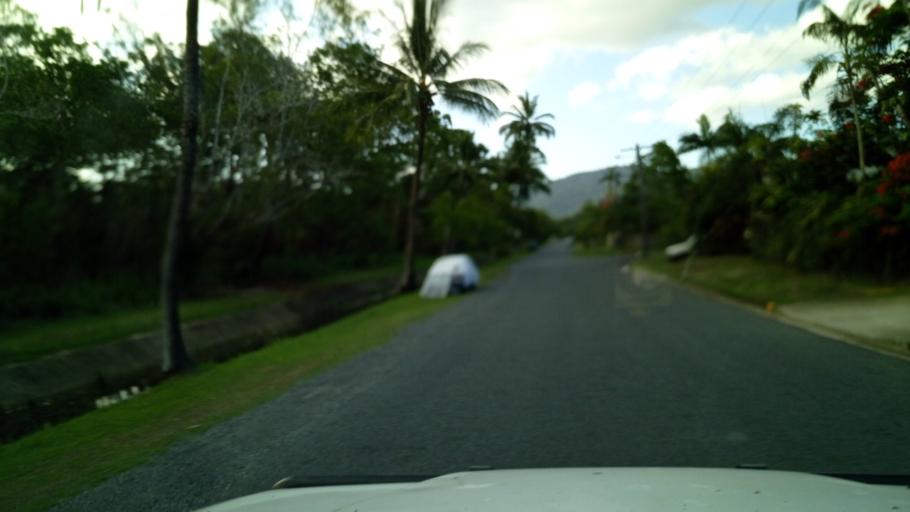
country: AU
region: Queensland
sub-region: Cairns
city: Cairns
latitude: -16.9171
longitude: 145.7548
